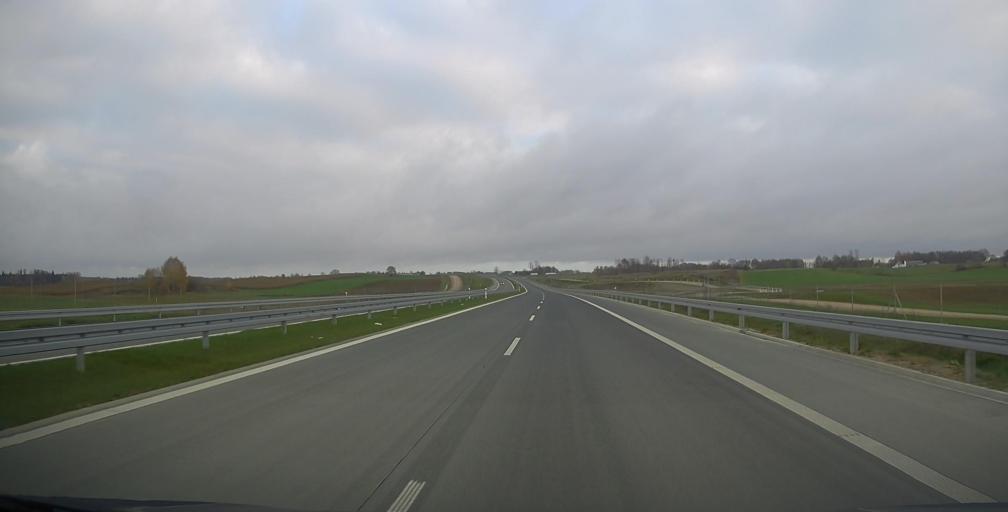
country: PL
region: Podlasie
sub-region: Powiat suwalski
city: Raczki
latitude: 53.9320
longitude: 22.7559
